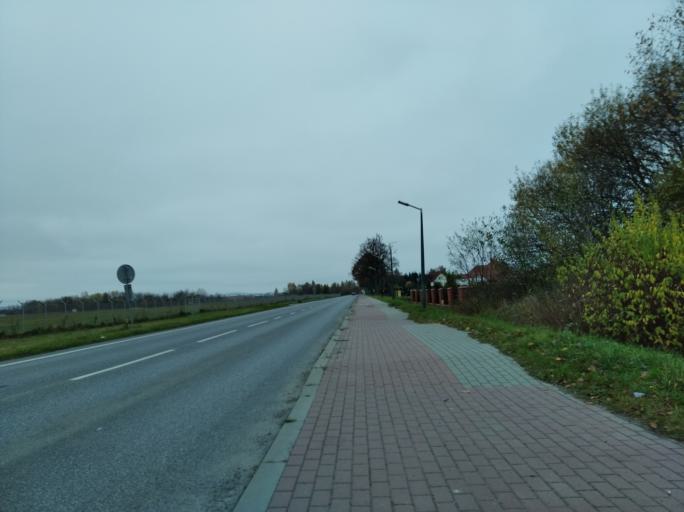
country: PL
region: Subcarpathian Voivodeship
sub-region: Krosno
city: Krosno
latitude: 49.6856
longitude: 21.7240
